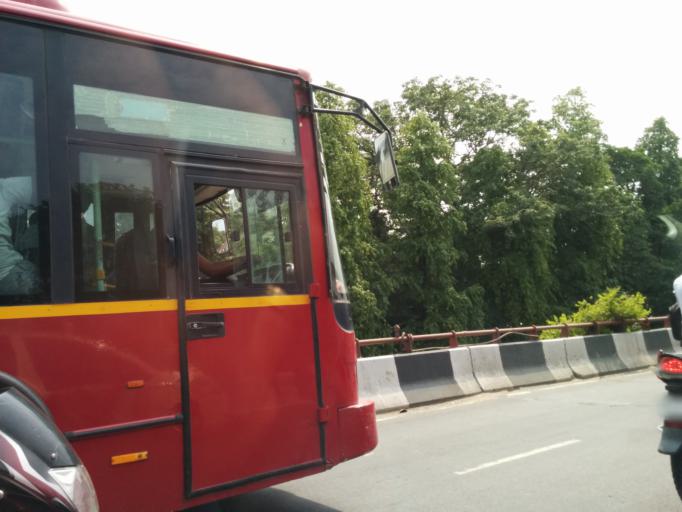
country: IN
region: NCT
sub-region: New Delhi
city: New Delhi
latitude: 28.5442
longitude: 77.2027
